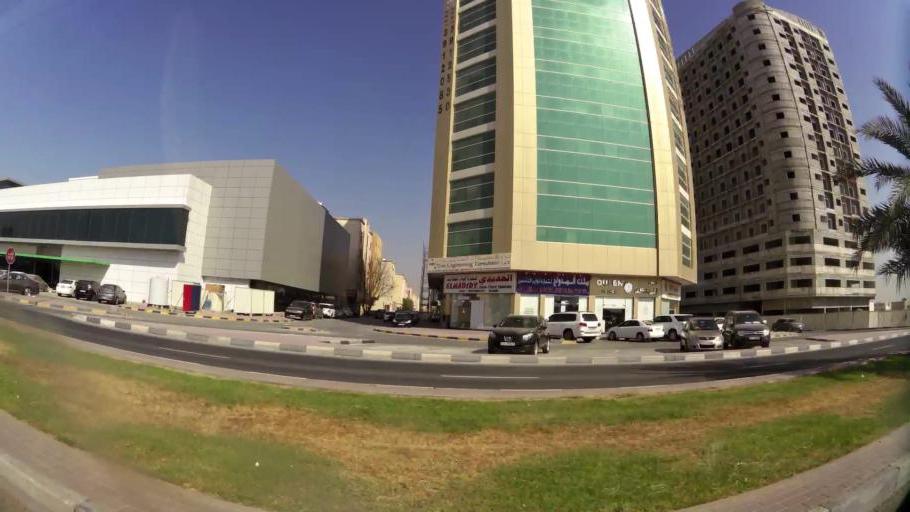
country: AE
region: Ajman
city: Ajman
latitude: 25.4017
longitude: 55.5048
